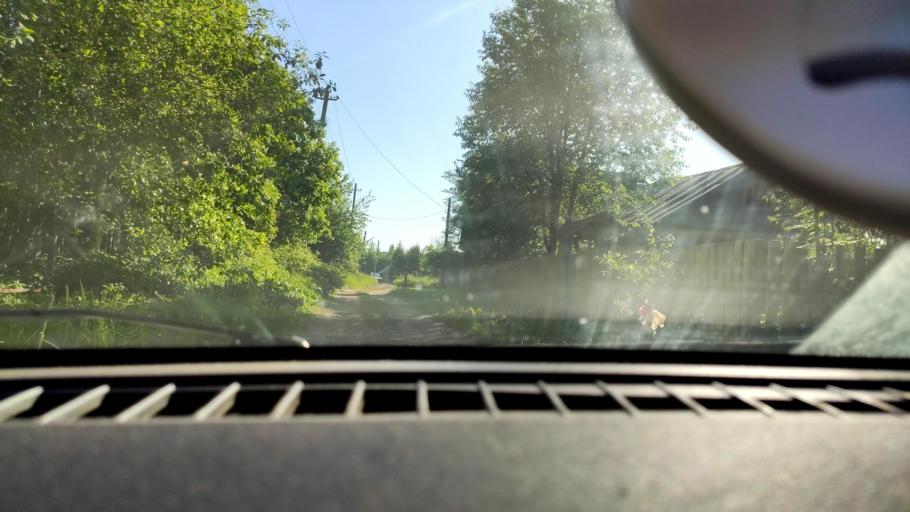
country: RU
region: Perm
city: Novyye Lyady
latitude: 58.1750
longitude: 56.5973
